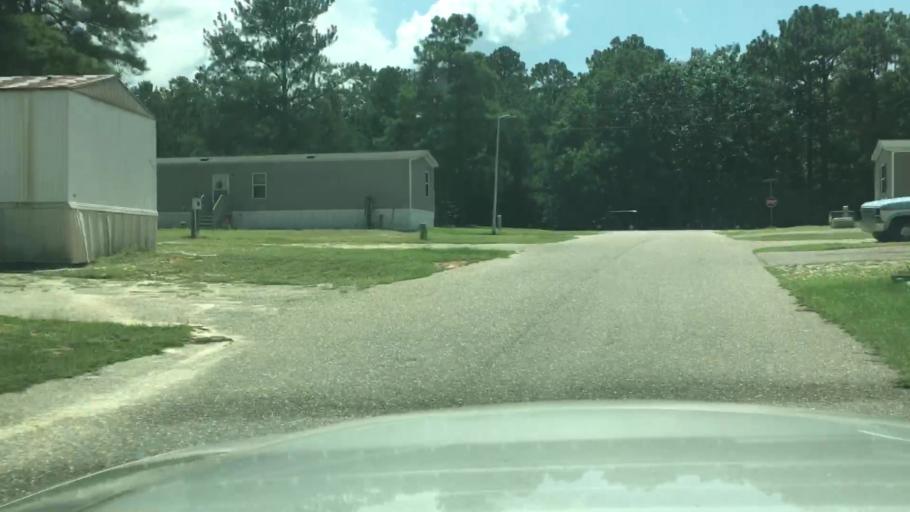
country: US
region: North Carolina
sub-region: Cumberland County
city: Hope Mills
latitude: 35.0118
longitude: -78.9682
